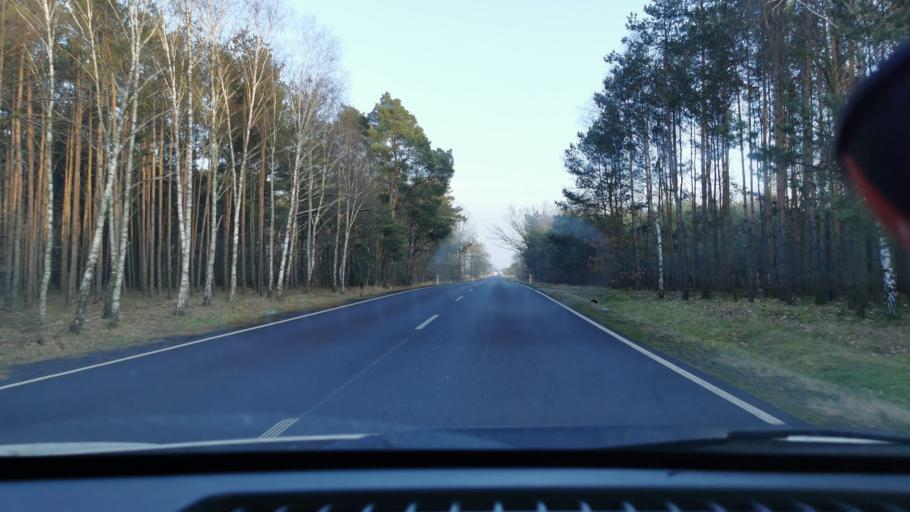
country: PL
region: Lodz Voivodeship
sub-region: Powiat pabianicki
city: Dlutow
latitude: 51.5113
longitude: 19.3567
